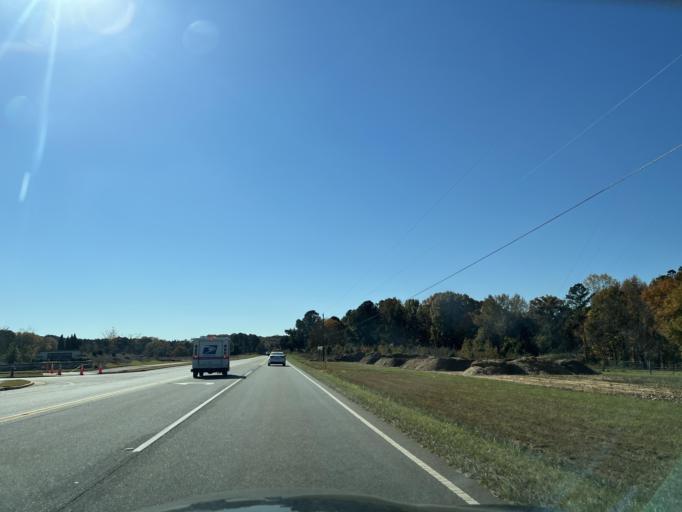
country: US
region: North Carolina
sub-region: Wake County
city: Fuquay-Varina
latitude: 35.6449
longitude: -78.7232
